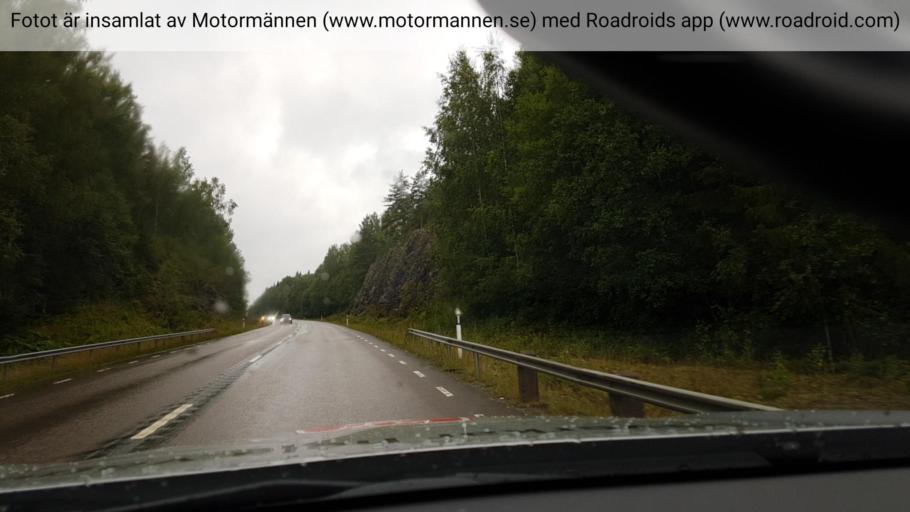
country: SE
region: Vaestra Goetaland
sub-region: Bengtsfors Kommun
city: Billingsfors
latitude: 58.9371
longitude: 12.1909
